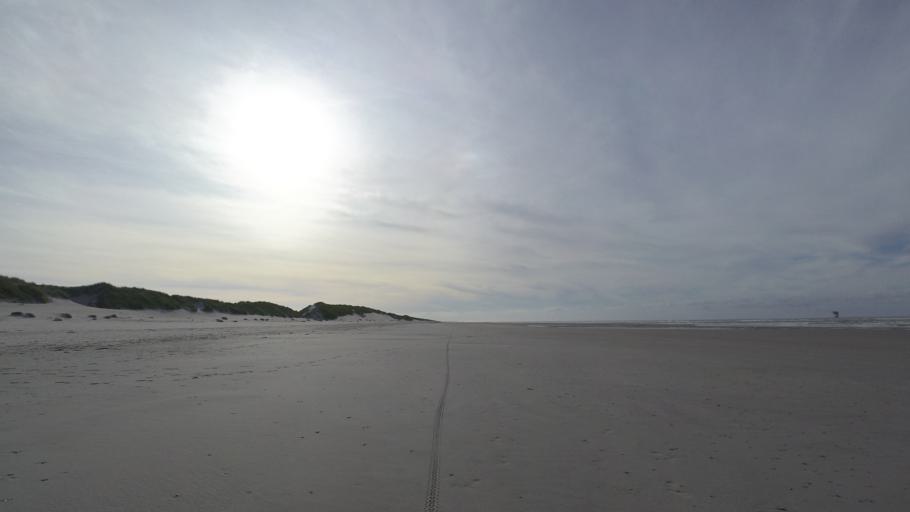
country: NL
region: Friesland
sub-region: Gemeente Dongeradeel
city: Holwerd
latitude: 53.4672
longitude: 5.8994
